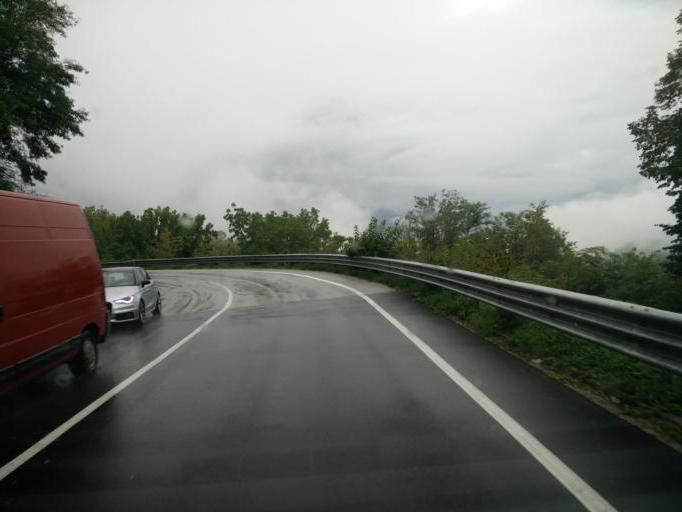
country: IT
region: Tuscany
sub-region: Provincia di Lucca
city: Fosciandora
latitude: 44.0882
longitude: 10.4535
